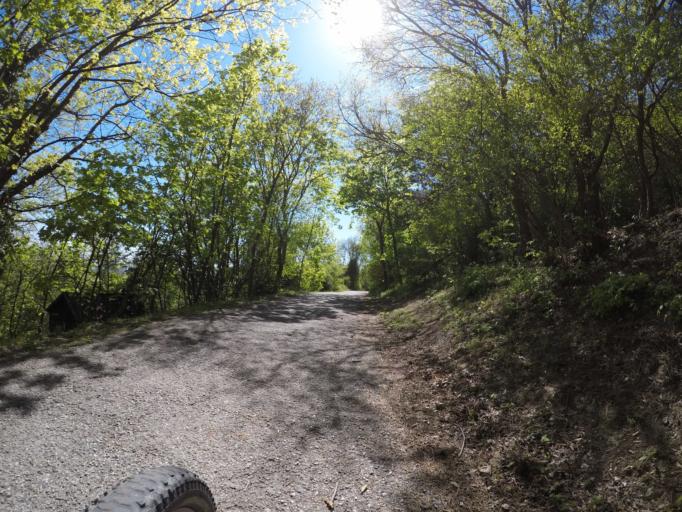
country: AT
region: Lower Austria
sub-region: Politischer Bezirk Modling
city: Modling
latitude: 48.0783
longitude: 16.2803
